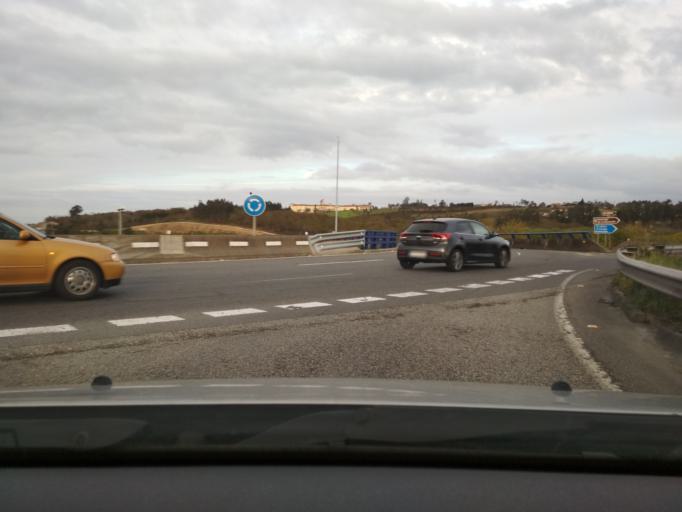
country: ES
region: Galicia
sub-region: Provincia da Coruna
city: Santiago de Compostela
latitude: 42.8985
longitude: -8.5105
